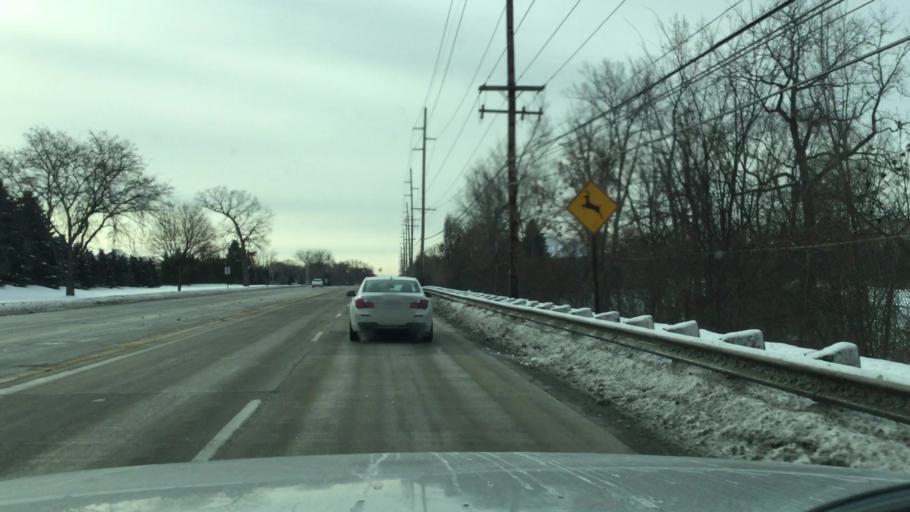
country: US
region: Michigan
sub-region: Oakland County
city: Troy
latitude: 42.6046
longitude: -83.1297
